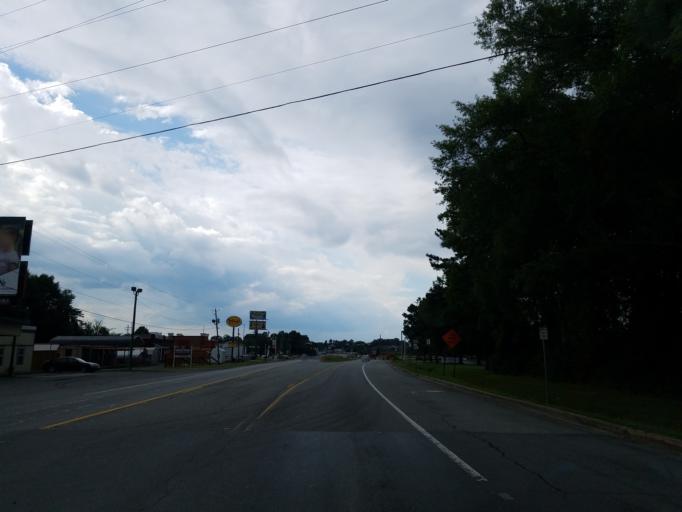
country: US
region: Georgia
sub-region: Bartow County
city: Adairsville
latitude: 34.3743
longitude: -84.9307
